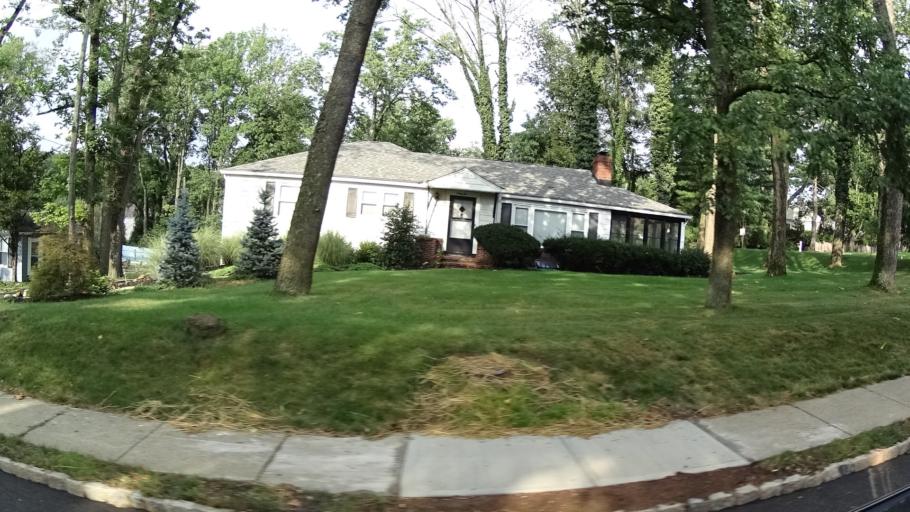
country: US
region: New Jersey
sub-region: Union County
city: New Providence
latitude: 40.7234
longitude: -74.4057
